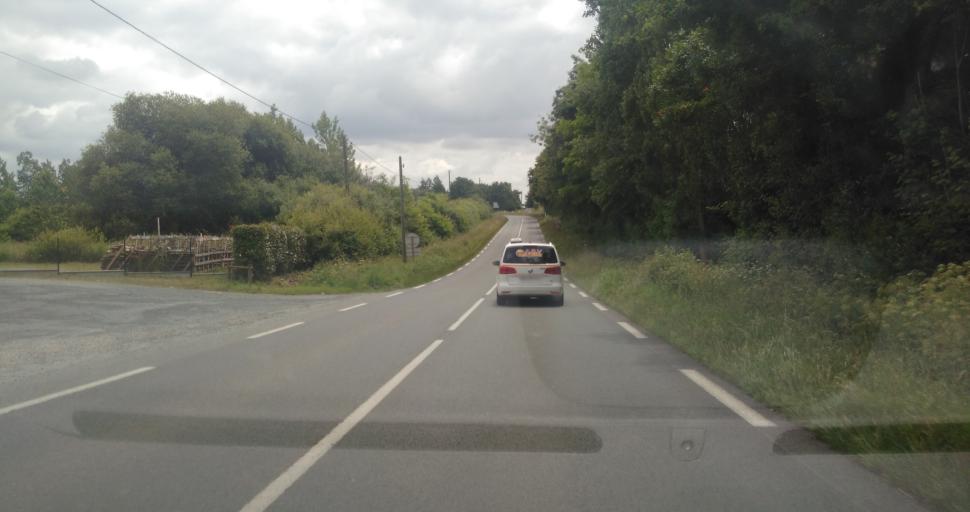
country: FR
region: Pays de la Loire
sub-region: Departement de la Vendee
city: Bournezeau
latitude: 46.5983
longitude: -1.1316
